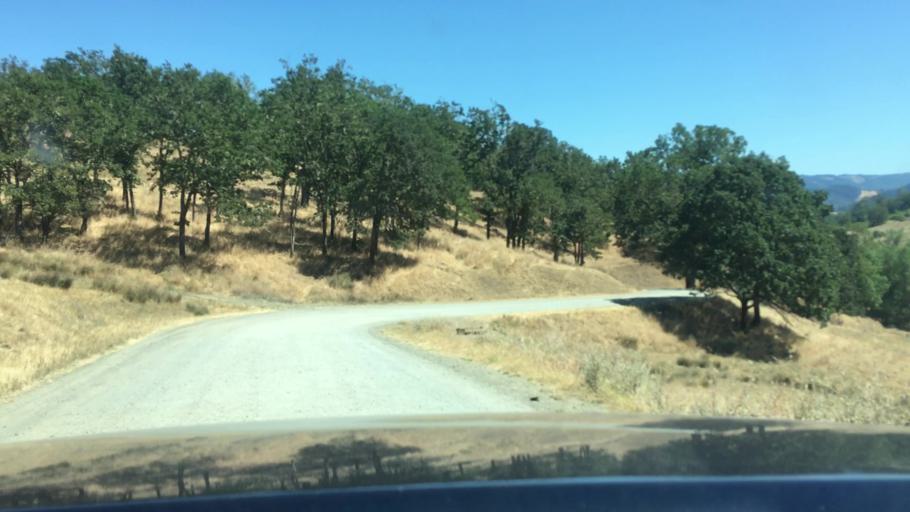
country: US
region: Oregon
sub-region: Douglas County
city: Winston
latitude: 43.1357
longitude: -123.4373
